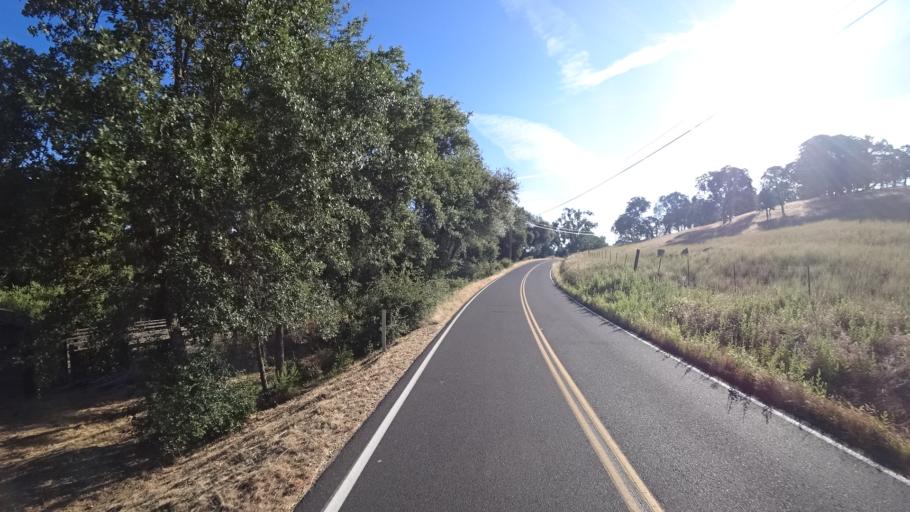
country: US
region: California
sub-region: Calaveras County
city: Valley Springs
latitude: 38.2135
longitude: -120.7735
